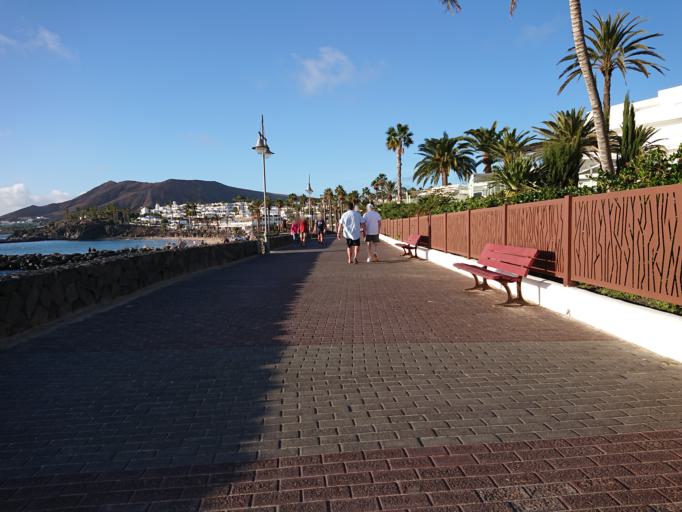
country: ES
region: Canary Islands
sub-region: Provincia de Las Palmas
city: Playa Blanca
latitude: 28.8565
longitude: -13.8404
